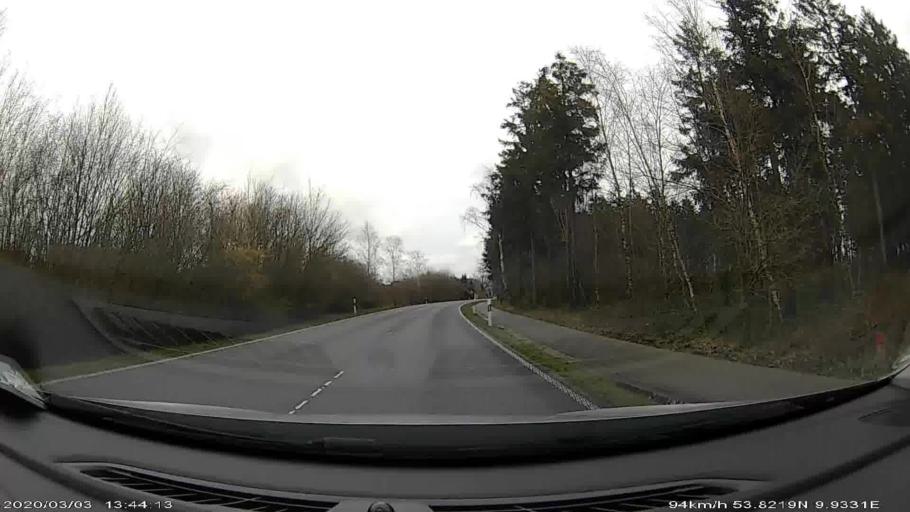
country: DE
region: Schleswig-Holstein
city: Kaltenkirchen
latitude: 53.8227
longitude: 9.9348
